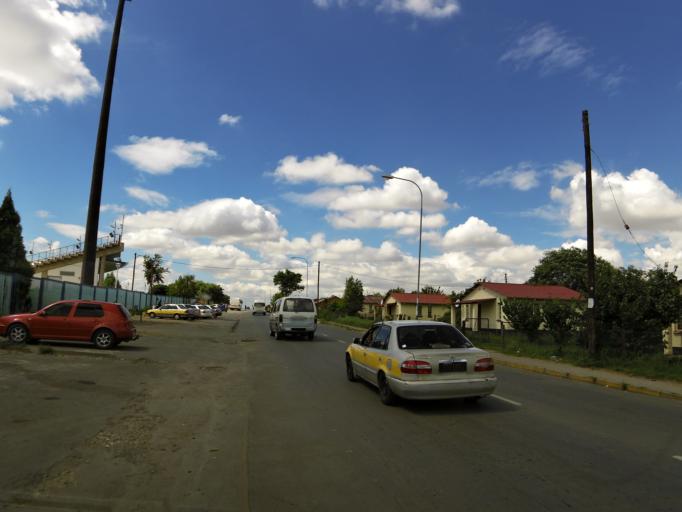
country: LS
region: Maseru
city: Maseru
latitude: -29.3113
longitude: 27.5003
